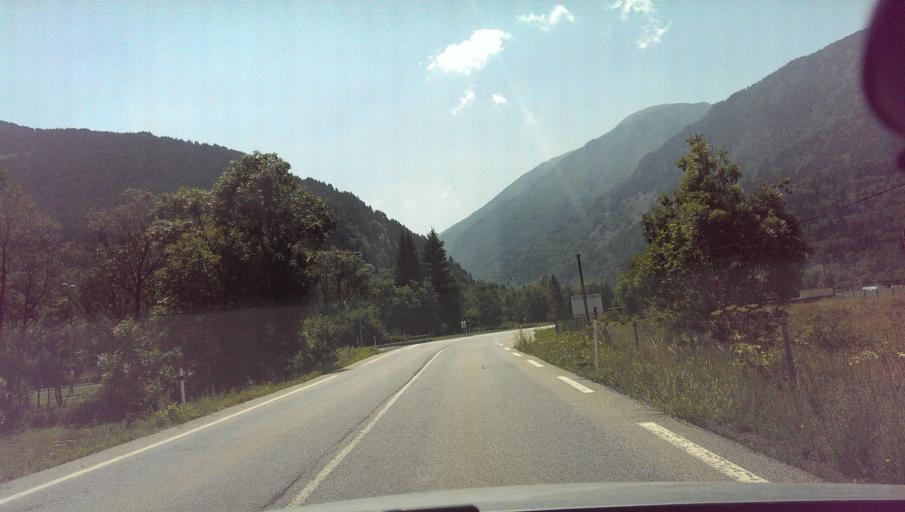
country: ES
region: Catalonia
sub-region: Provincia de Girona
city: Meranges
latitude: 42.5235
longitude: 1.8228
